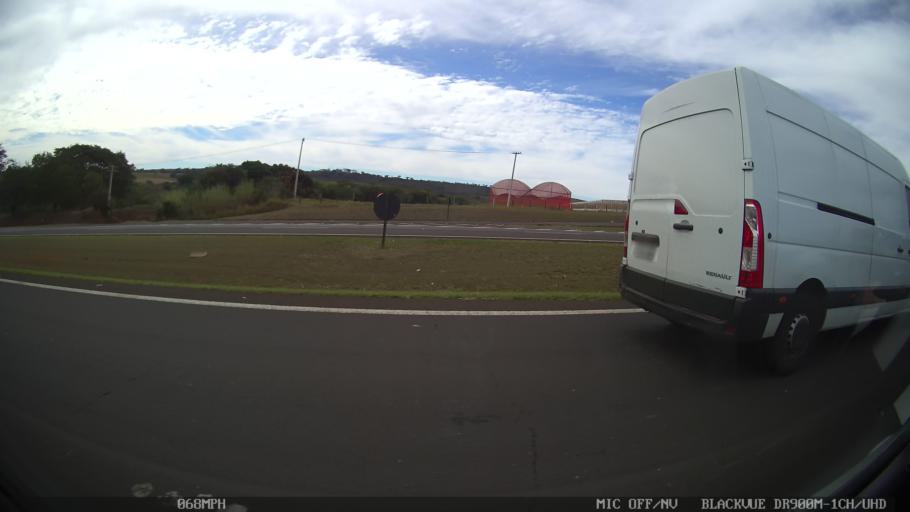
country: BR
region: Sao Paulo
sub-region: Santa Adelia
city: Santa Adelia
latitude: -21.2991
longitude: -48.8353
